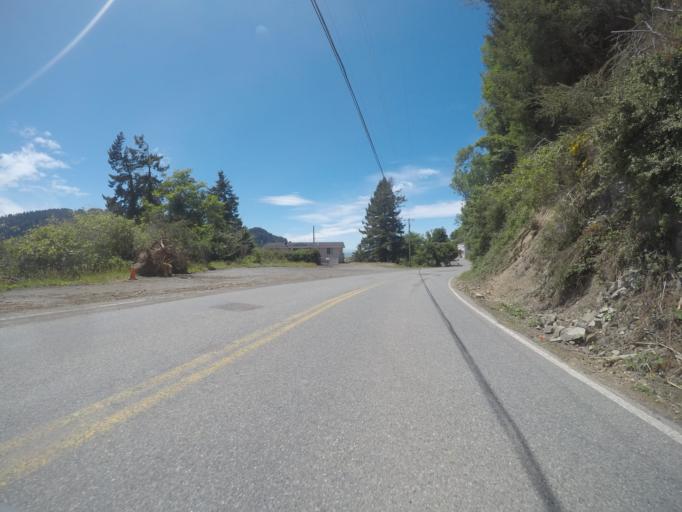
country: US
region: California
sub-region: Del Norte County
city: Bertsch-Oceanview
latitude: 41.5477
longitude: -124.0620
